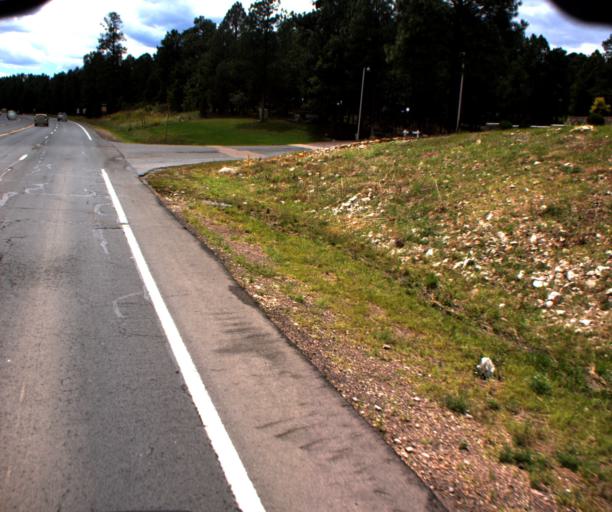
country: US
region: Arizona
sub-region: Navajo County
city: Show Low
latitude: 34.2260
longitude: -110.0288
